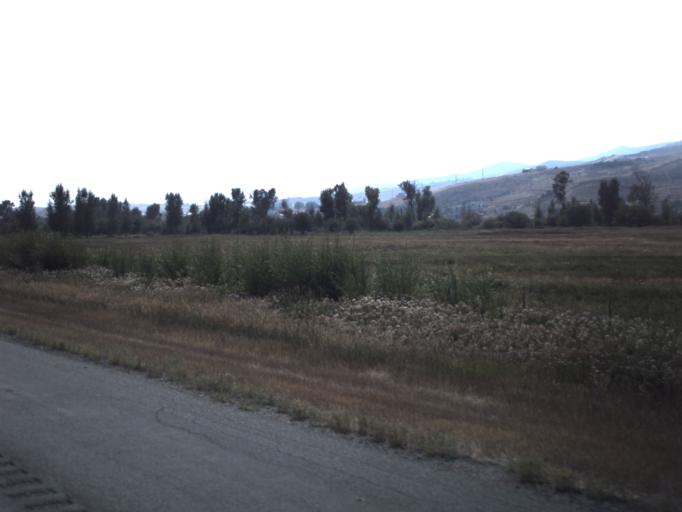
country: US
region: Utah
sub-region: Summit County
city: Coalville
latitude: 40.8688
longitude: -111.3895
